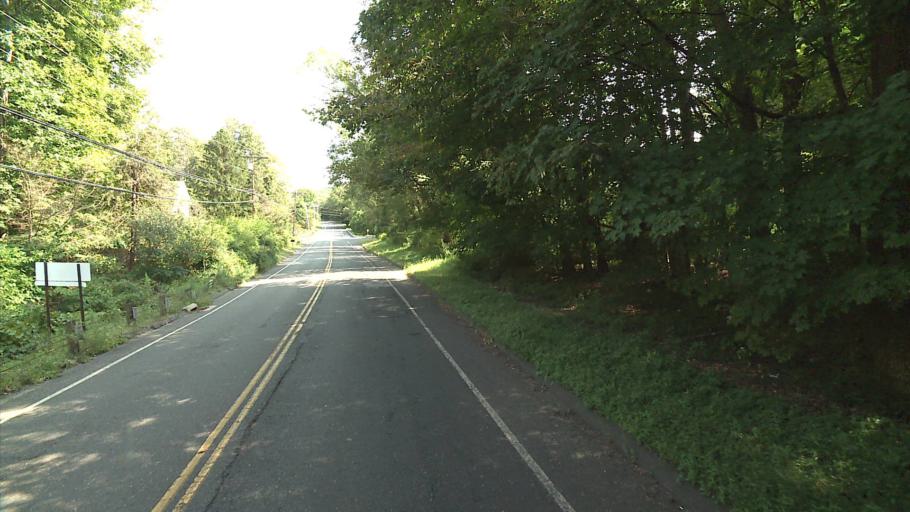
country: US
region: Connecticut
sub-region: New Haven County
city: Heritage Village
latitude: 41.4634
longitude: -73.2440
